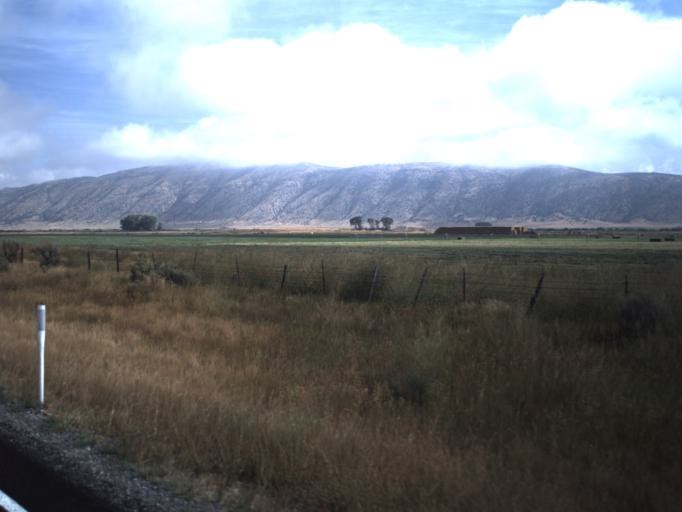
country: US
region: Utah
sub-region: Rich County
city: Randolph
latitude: 41.5464
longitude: -111.1567
